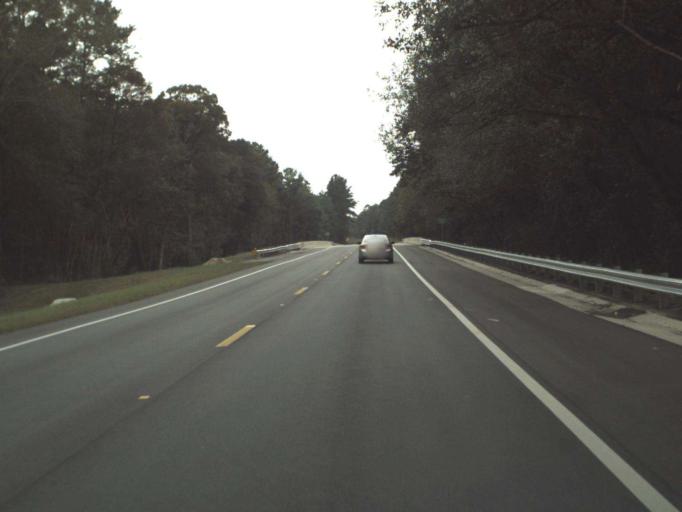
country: US
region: Florida
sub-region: Calhoun County
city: Blountstown
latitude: 30.5304
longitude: -85.0297
